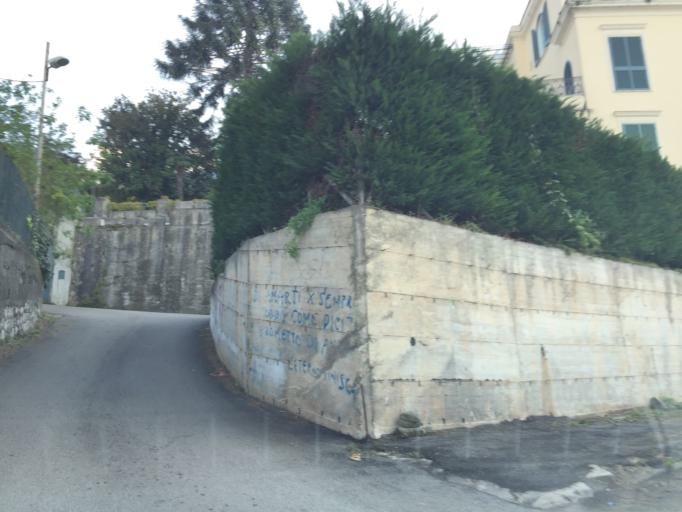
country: IT
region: Campania
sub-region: Provincia di Napoli
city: Castellammare di Stabia
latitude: 40.6870
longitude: 14.4853
